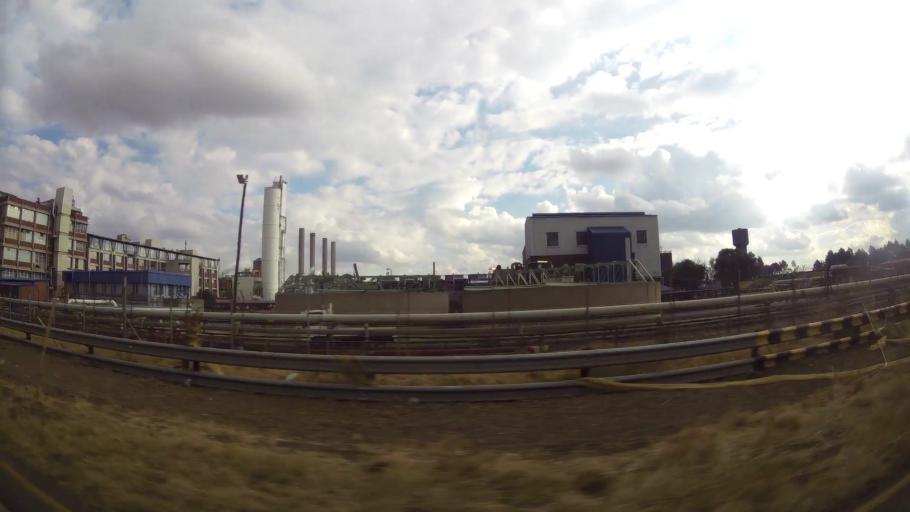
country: ZA
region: Orange Free State
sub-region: Fezile Dabi District Municipality
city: Sasolburg
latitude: -26.8190
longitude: 27.8437
